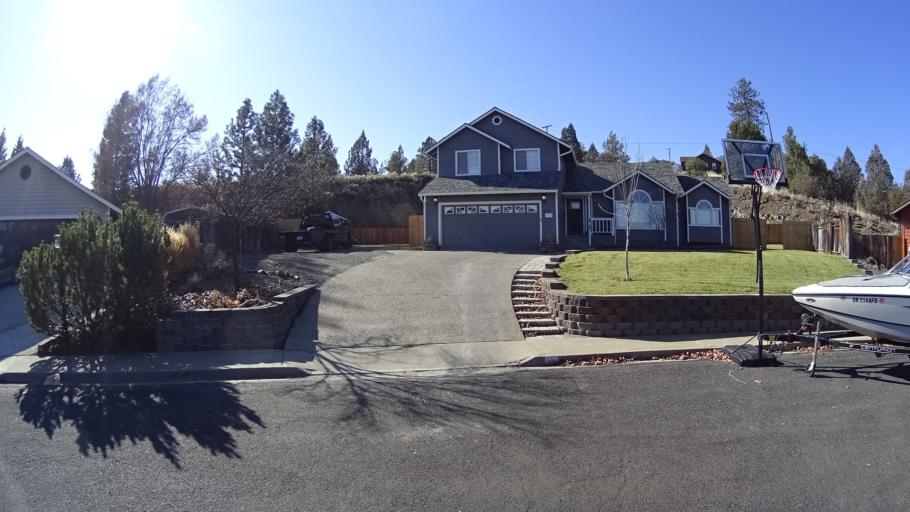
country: US
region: California
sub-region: Siskiyou County
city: Yreka
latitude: 41.7293
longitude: -122.6503
